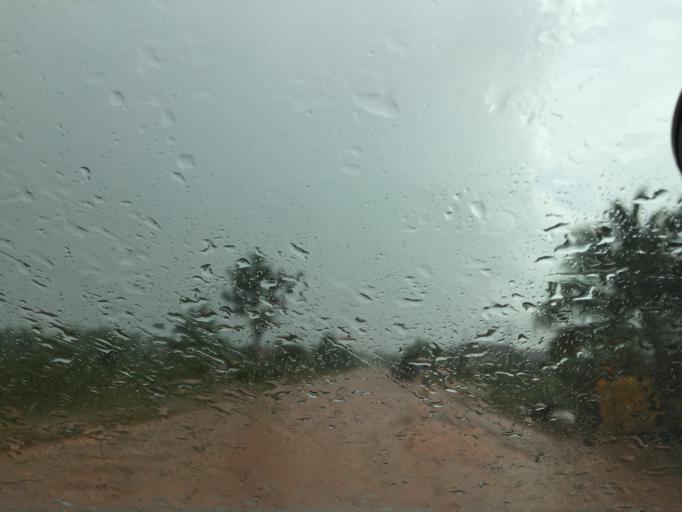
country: LA
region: Attapu
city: Attapu
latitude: 14.8220
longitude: 106.7950
